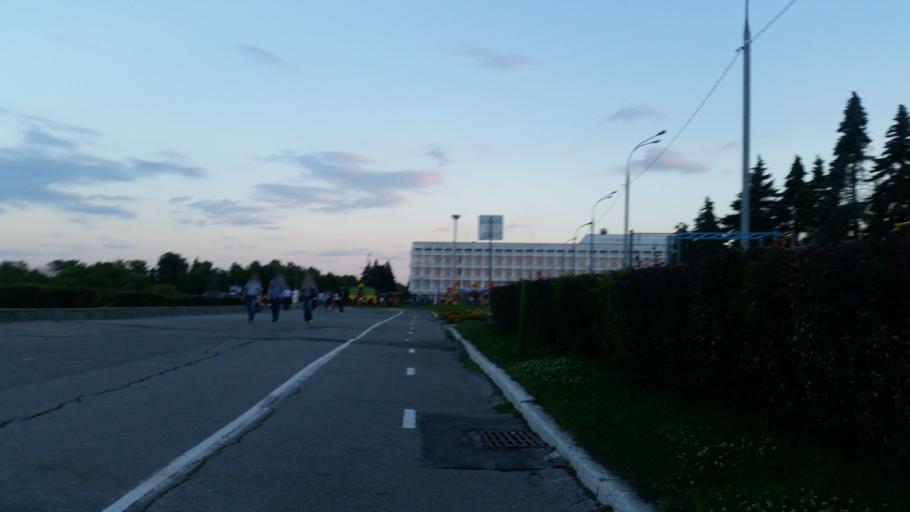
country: RU
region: Ulyanovsk
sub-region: Ulyanovskiy Rayon
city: Ulyanovsk
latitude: 54.3197
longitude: 48.4080
